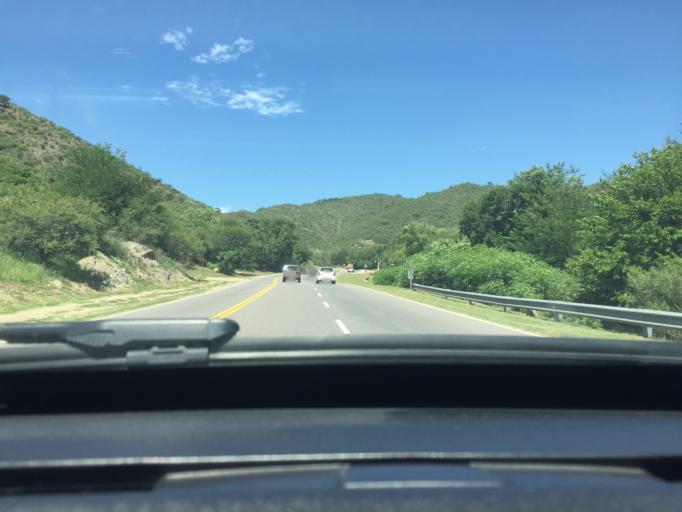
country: AR
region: Cordoba
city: Alta Gracia
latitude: -31.7411
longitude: -64.4592
